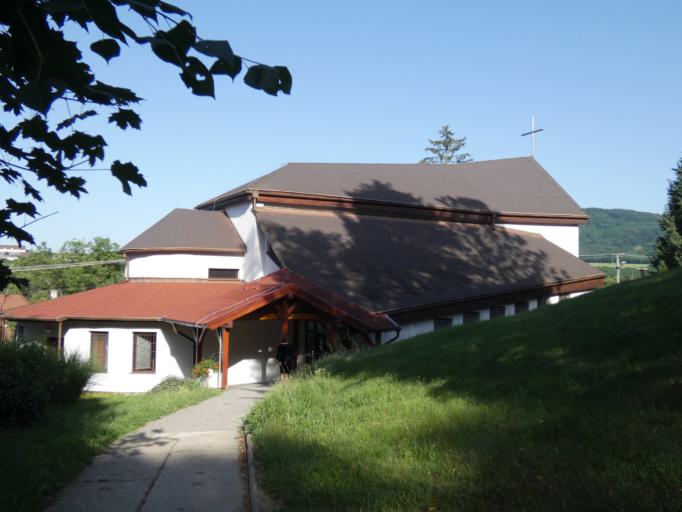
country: SK
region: Banskobystricky
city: Velky Krtis
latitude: 48.2101
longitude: 19.3420
